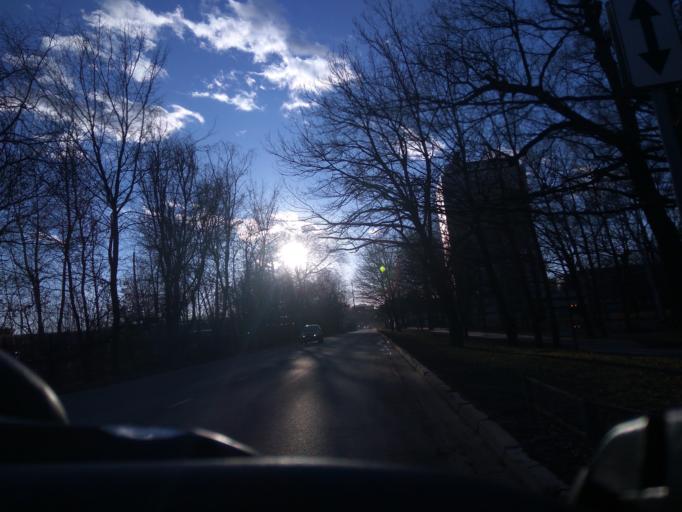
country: RU
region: Moscow
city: Ostankinskiy
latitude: 55.8181
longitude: 37.6088
